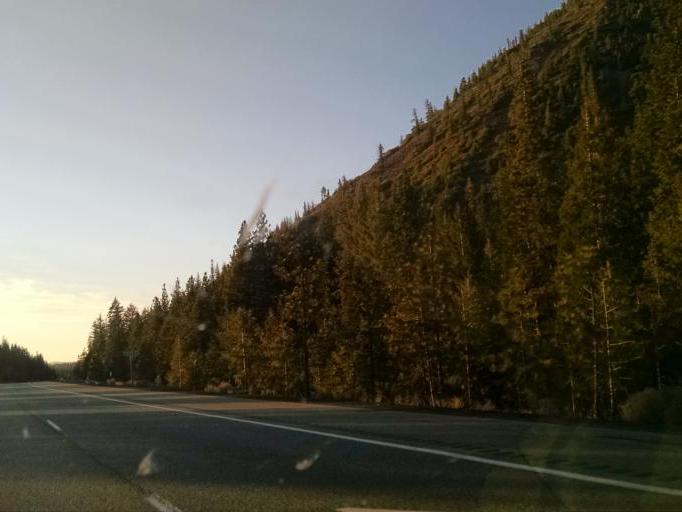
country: US
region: California
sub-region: Siskiyou County
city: Mount Shasta
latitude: 41.3553
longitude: -122.3562
